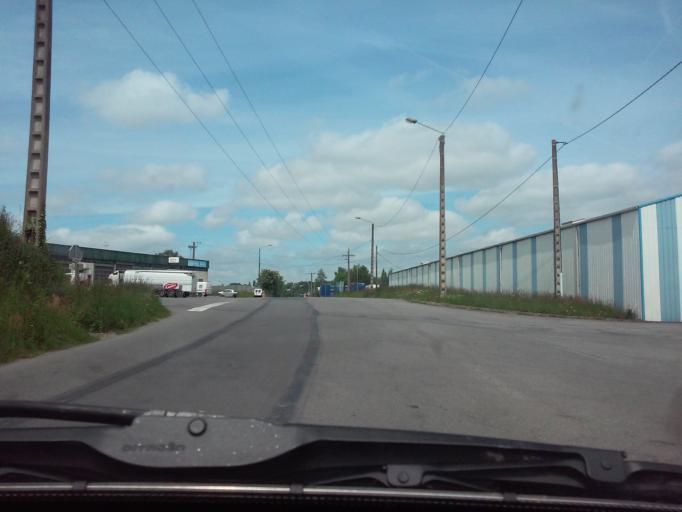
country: FR
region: Brittany
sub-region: Departement d'Ille-et-Vilaine
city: Beauce
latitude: 48.3323
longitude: -1.1648
